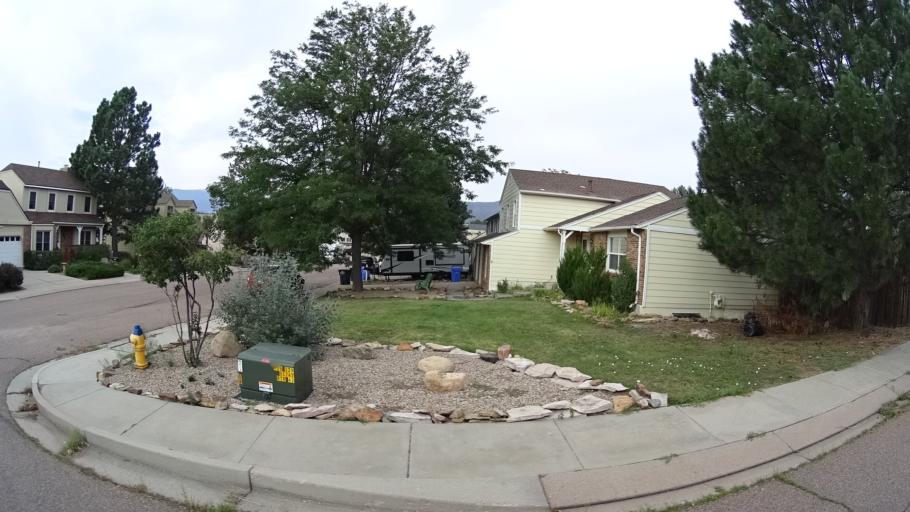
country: US
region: Colorado
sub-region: El Paso County
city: Air Force Academy
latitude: 38.9245
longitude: -104.8366
